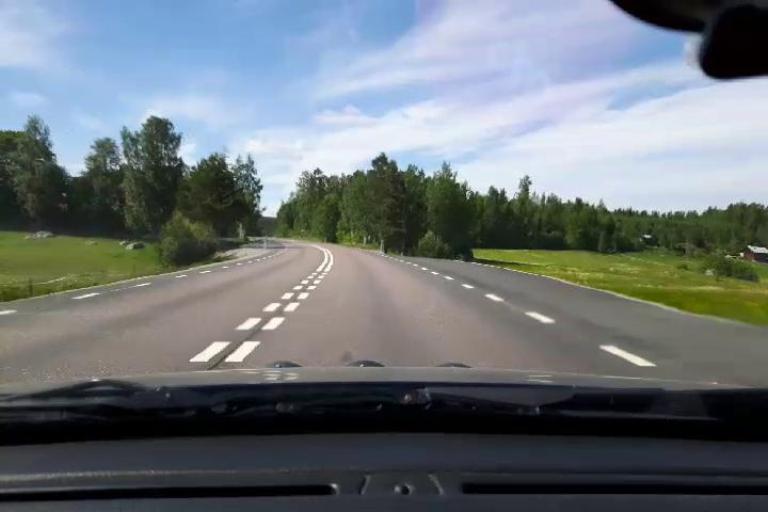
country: SE
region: Gaevleborg
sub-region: Bollnas Kommun
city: Kilafors
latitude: 61.1766
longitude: 16.7927
